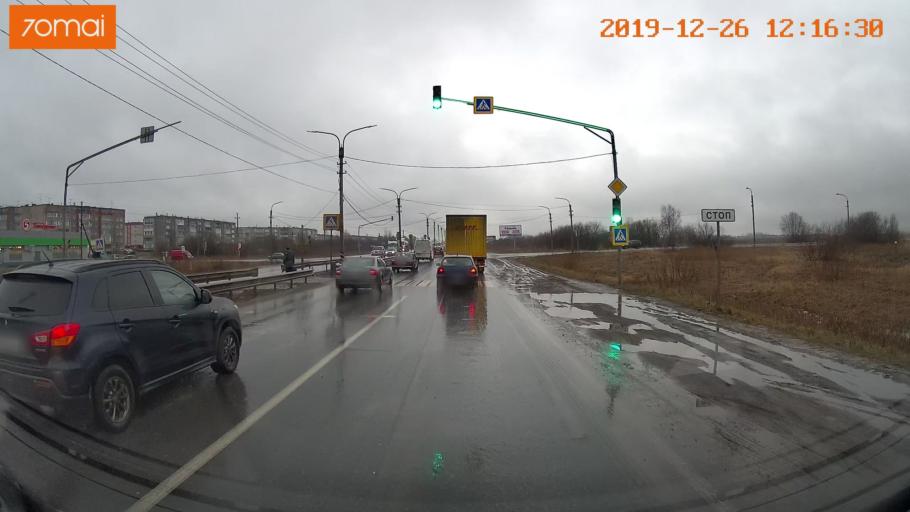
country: RU
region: Vologda
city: Tonshalovo
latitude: 59.1975
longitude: 37.9425
